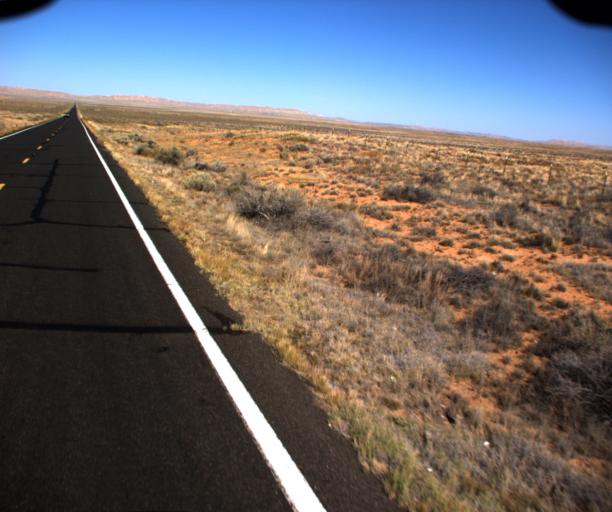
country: US
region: Arizona
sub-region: Navajo County
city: First Mesa
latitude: 35.6733
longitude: -110.4976
